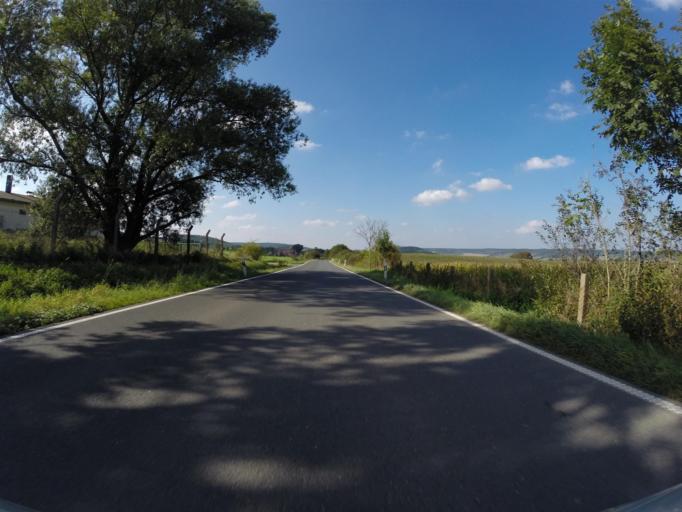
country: DE
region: Thuringia
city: Schongleina
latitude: 50.9242
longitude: 11.7280
